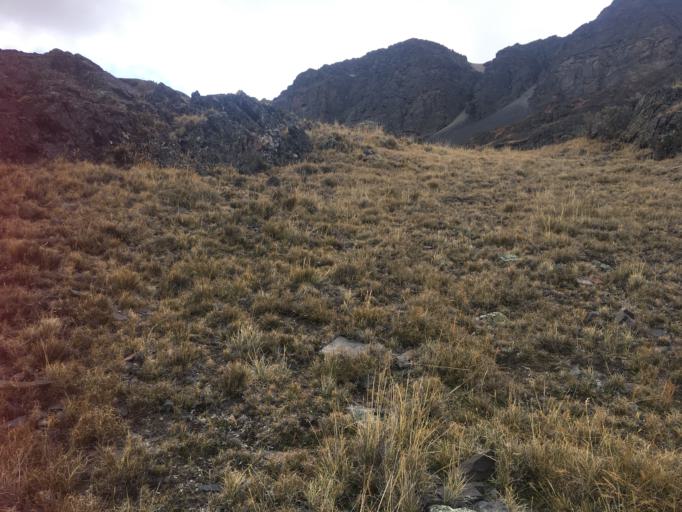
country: BO
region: La Paz
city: La Paz
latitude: -16.3942
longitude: -67.9692
